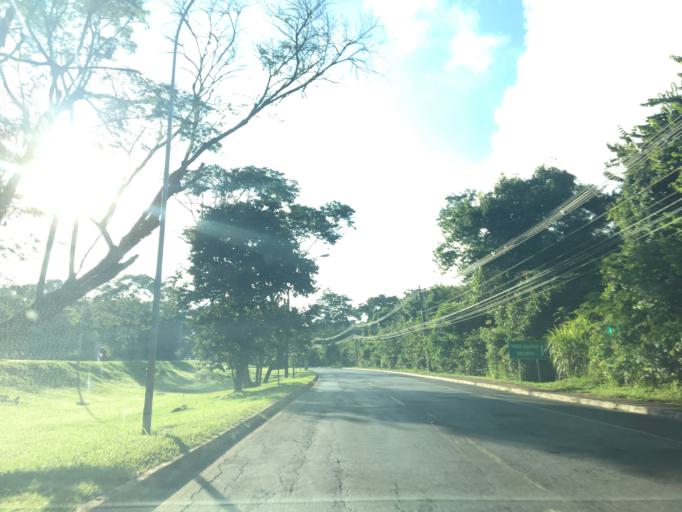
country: BR
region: Federal District
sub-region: Brasilia
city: Brasilia
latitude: -15.8353
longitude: -47.8206
